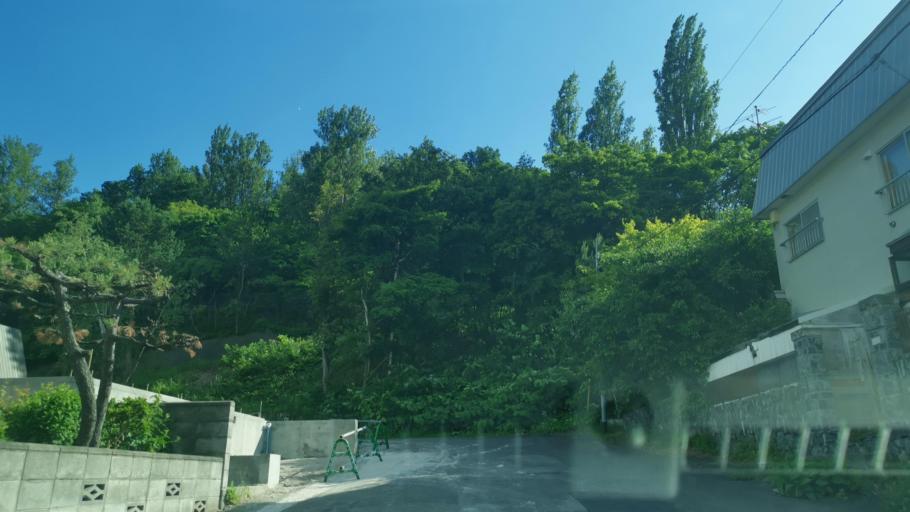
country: JP
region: Hokkaido
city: Sapporo
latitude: 43.0699
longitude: 141.2838
